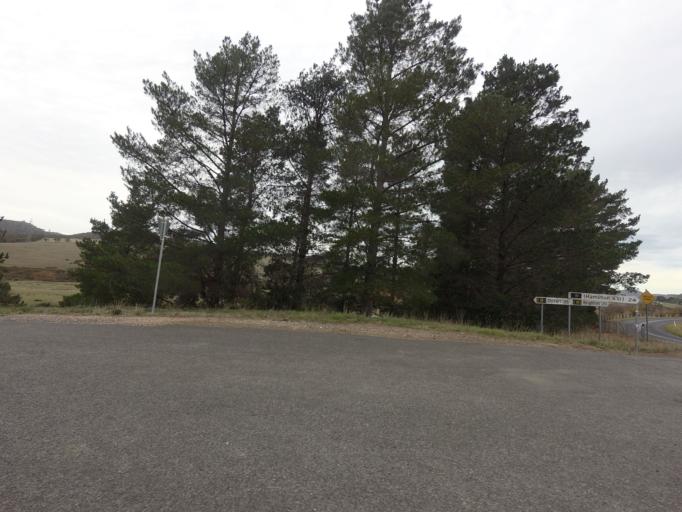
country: AU
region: Tasmania
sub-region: Derwent Valley
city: New Norfolk
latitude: -42.6030
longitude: 147.0758
